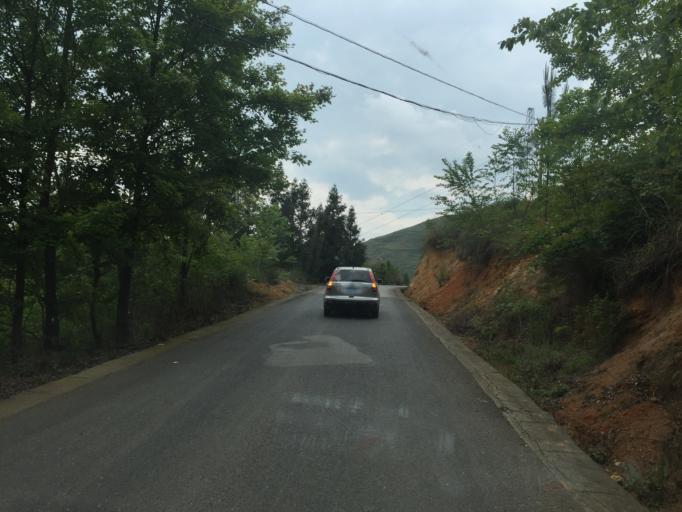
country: CN
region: Guangxi Zhuangzu Zizhiqu
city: Xinzhou
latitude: 25.6519
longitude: 105.2370
